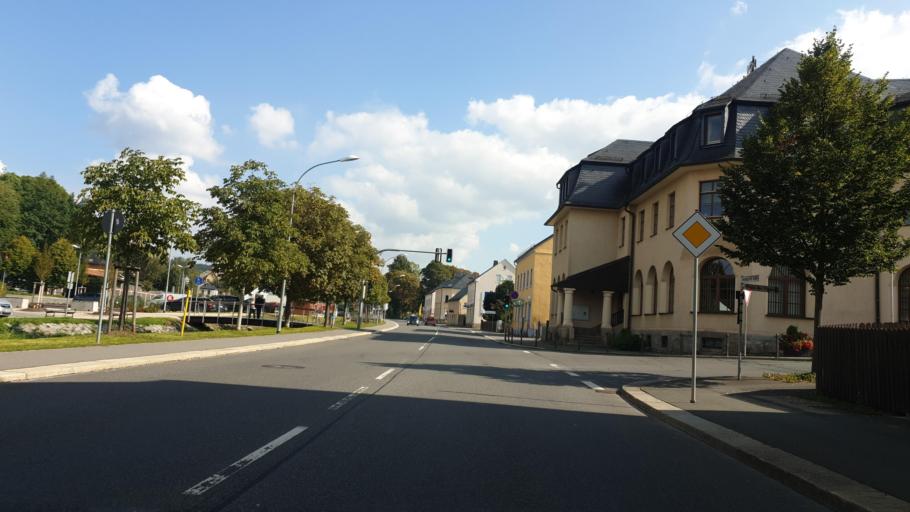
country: DE
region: Saxony
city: Rodewisch
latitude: 50.5312
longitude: 12.4123
